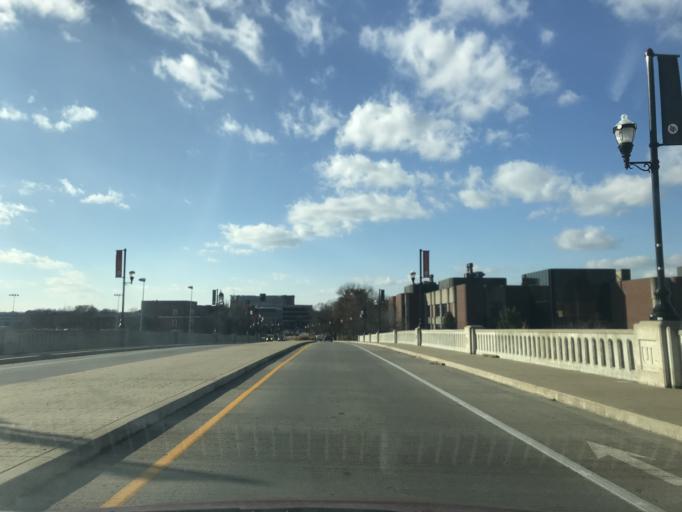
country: US
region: Kentucky
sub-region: Jefferson County
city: Audubon Park
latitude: 38.2133
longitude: -85.7566
